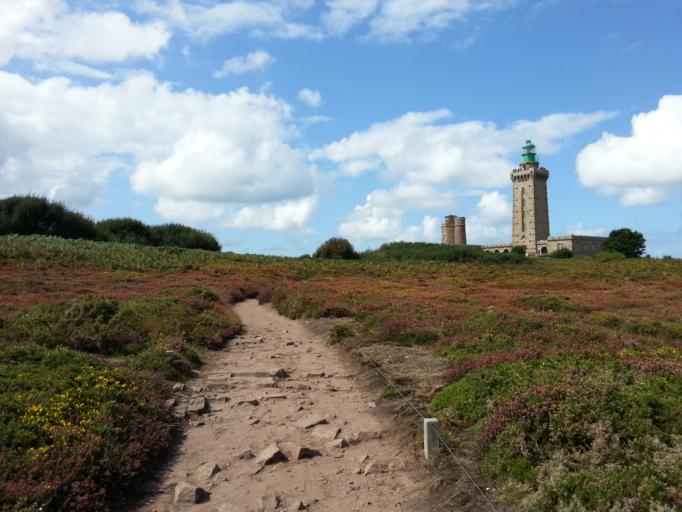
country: FR
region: Brittany
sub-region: Departement des Cotes-d'Armor
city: Saint-Cast-le-Guildo
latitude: 48.6830
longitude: -2.3175
